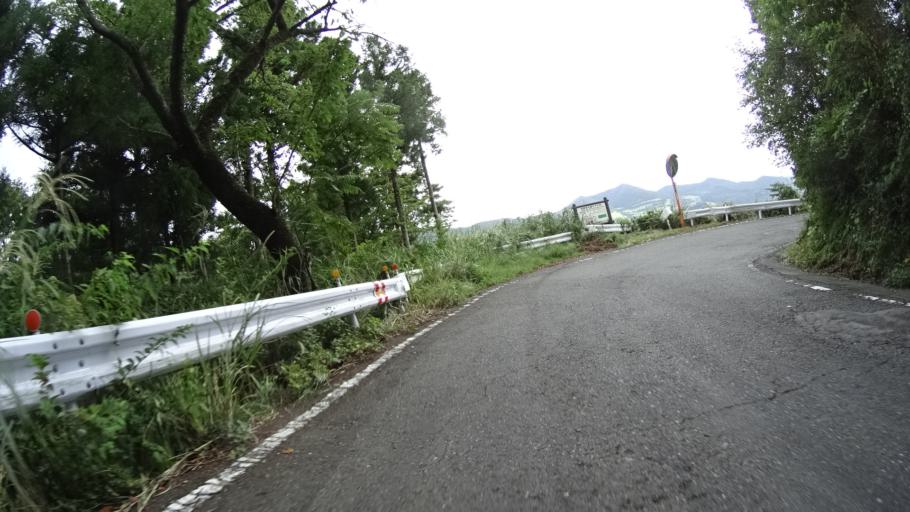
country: JP
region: Kanagawa
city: Hadano
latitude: 35.4107
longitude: 139.2153
